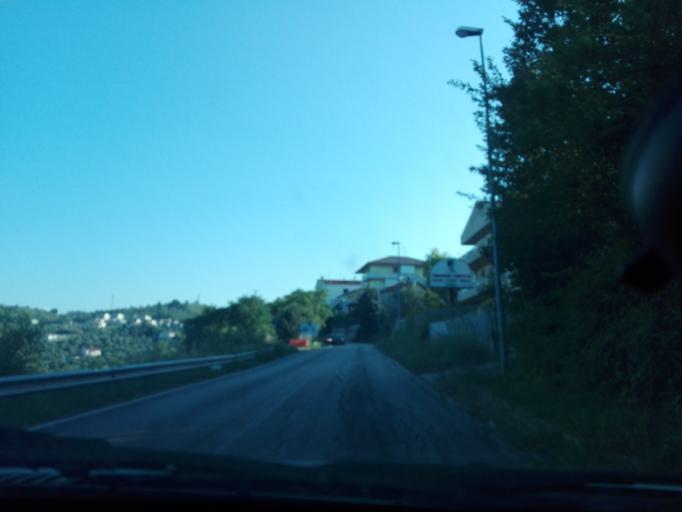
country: IT
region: Abruzzo
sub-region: Provincia di Pescara
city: Cappelle sul Tavo
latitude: 42.4694
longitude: 14.1057
